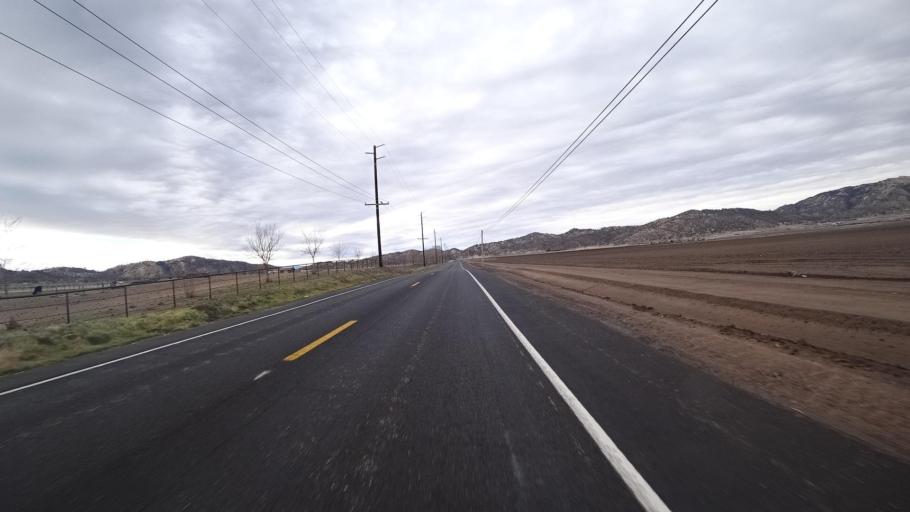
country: US
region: California
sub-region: Kern County
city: Stallion Springs
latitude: 35.0946
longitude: -118.6066
